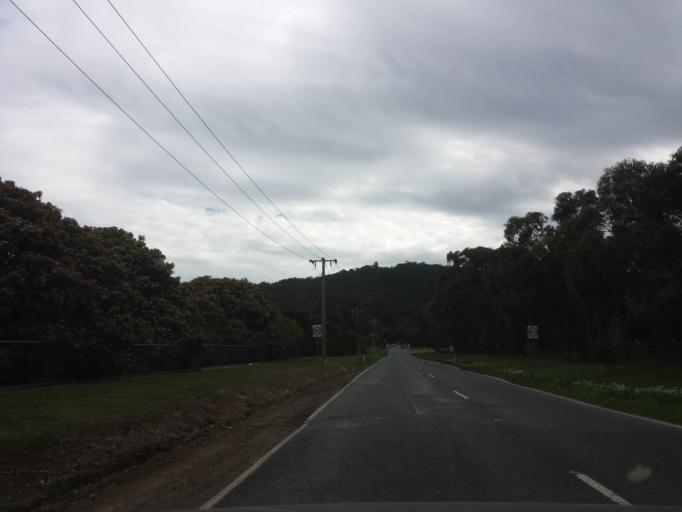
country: AU
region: Victoria
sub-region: Yarra Ranges
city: Yarra Glen
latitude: -37.6467
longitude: 145.3667
